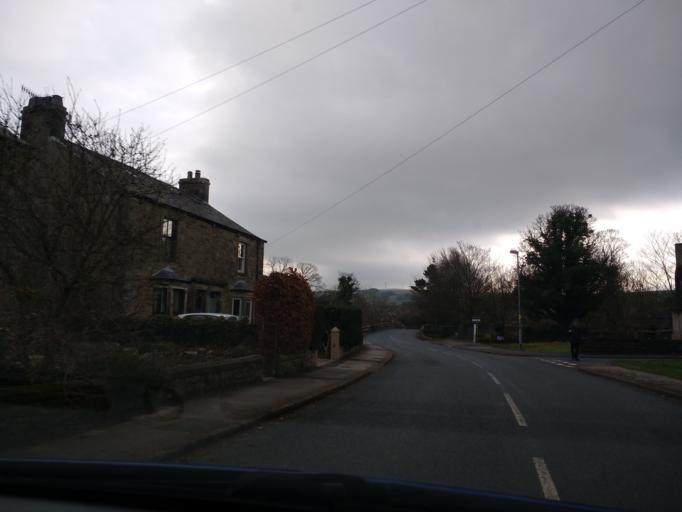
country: GB
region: England
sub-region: Lancashire
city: Caton
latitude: 54.0741
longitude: -2.7144
